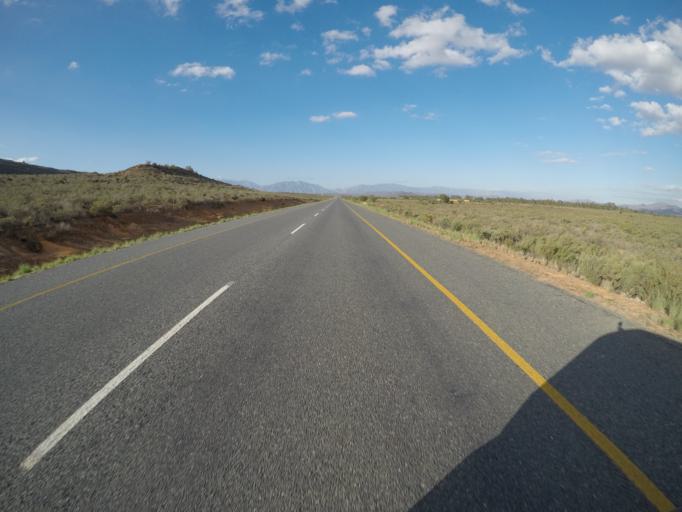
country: ZA
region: Western Cape
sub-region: Cape Winelands District Municipality
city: Worcester
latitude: -33.7824
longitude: 19.4608
